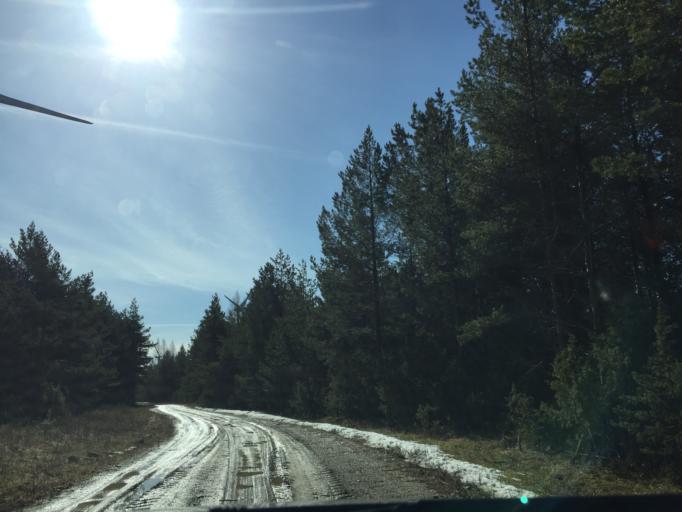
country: EE
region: Laeaene
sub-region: Haapsalu linn
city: Haapsalu
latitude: 58.6380
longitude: 23.5195
